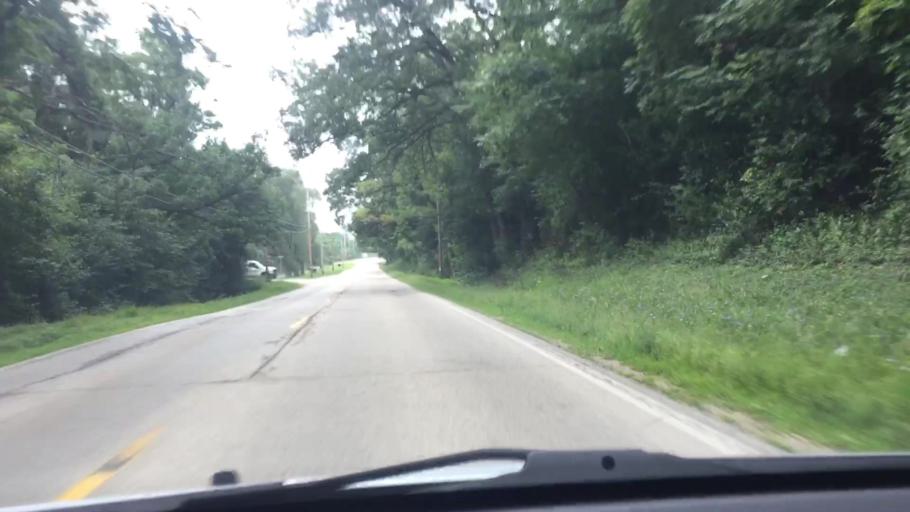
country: US
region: Wisconsin
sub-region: Waukesha County
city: Dousman
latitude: 43.0407
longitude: -88.4425
